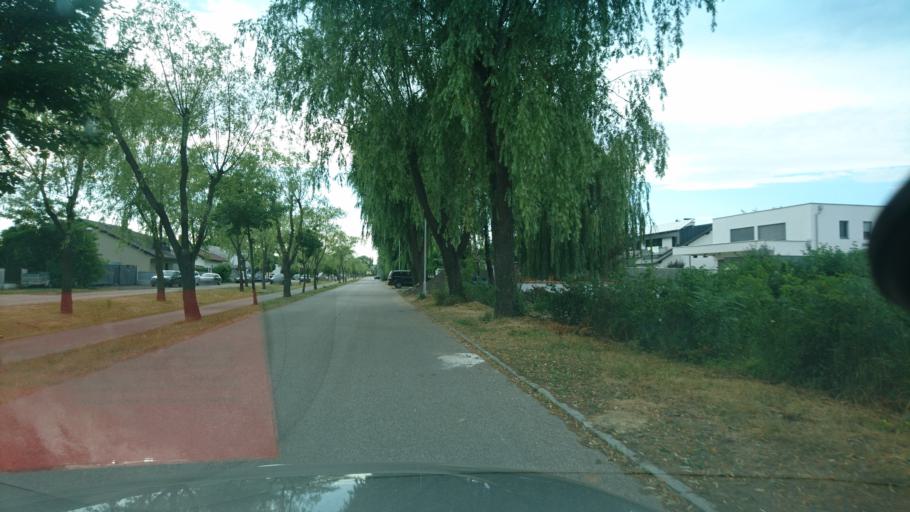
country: AT
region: Burgenland
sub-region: Politischer Bezirk Neusiedl am See
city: Neusiedl am See
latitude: 47.9357
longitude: 16.8495
